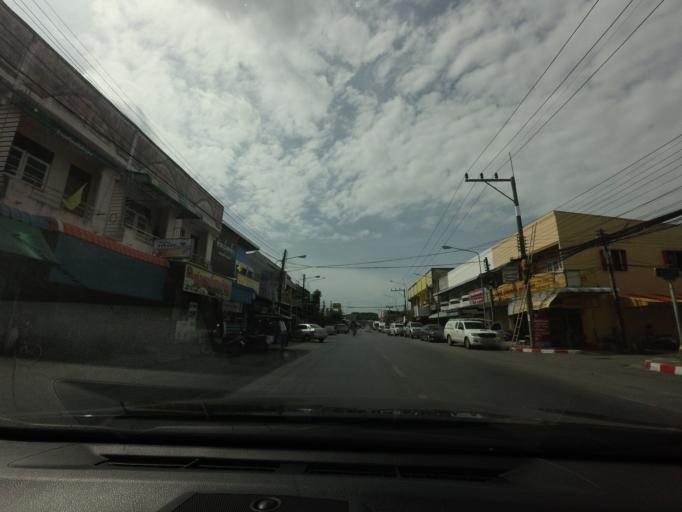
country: TH
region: Pattani
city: Pattani
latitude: 6.8751
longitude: 101.2487
